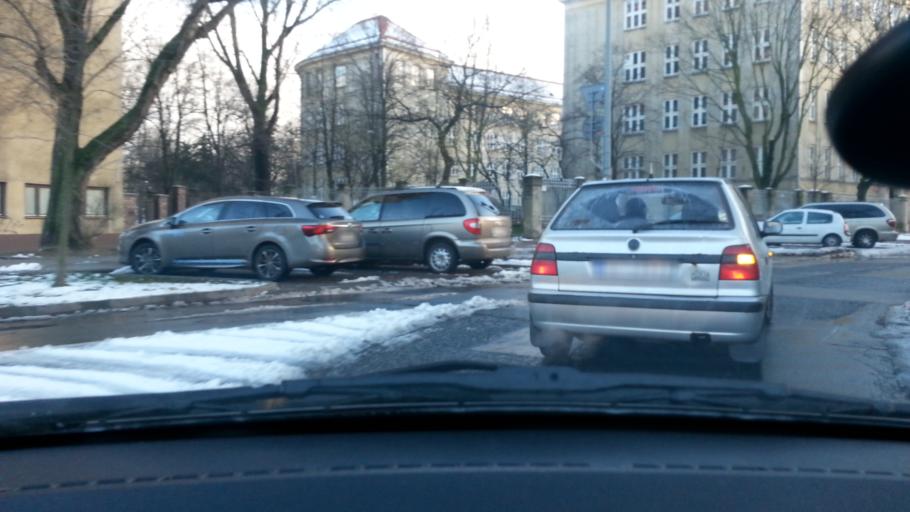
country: PL
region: Masovian Voivodeship
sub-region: Warszawa
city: Ochota
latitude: 52.2316
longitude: 20.9589
